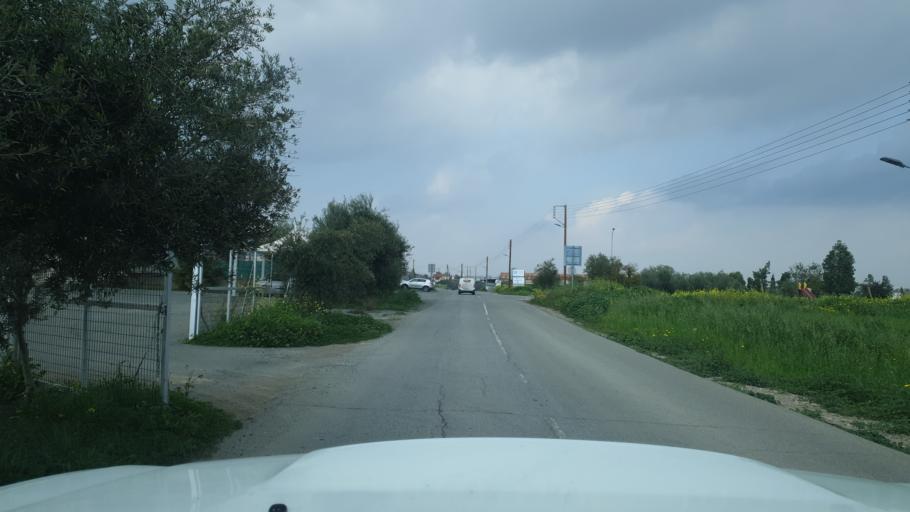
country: CY
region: Lefkosia
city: Geri
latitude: 35.0840
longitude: 33.3888
